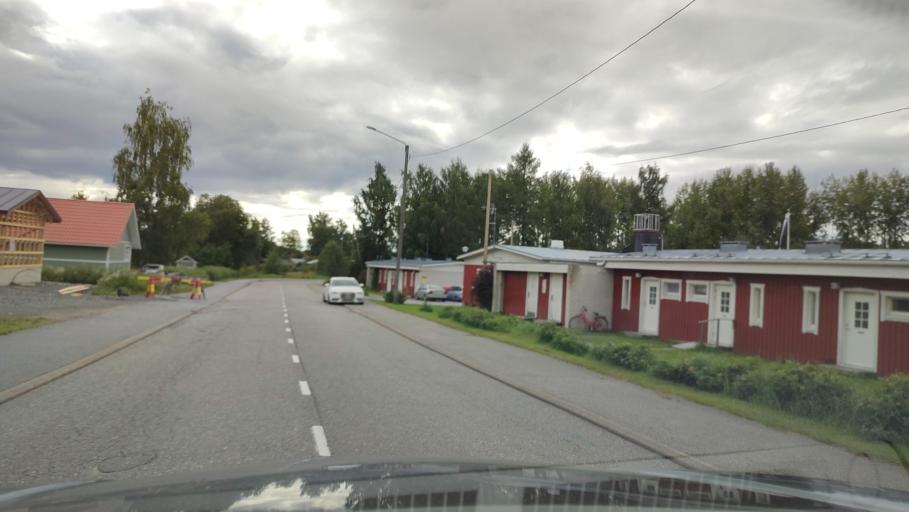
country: FI
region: Ostrobothnia
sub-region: Sydosterbotten
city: Kristinestad
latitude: 62.2696
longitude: 21.3669
